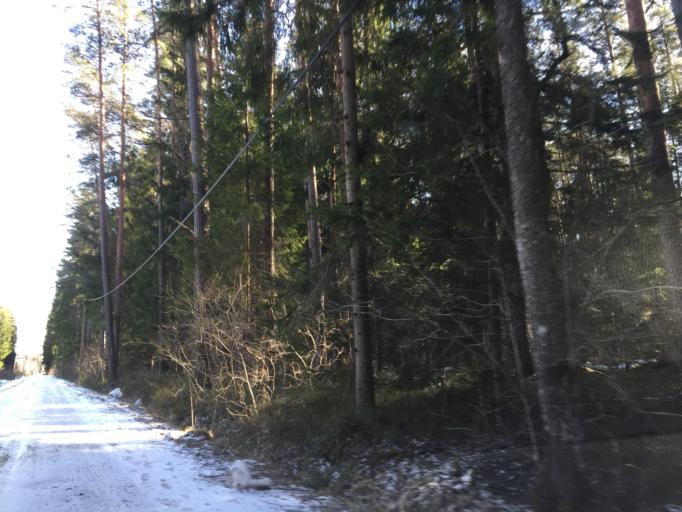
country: LV
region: Garkalne
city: Garkalne
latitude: 56.9521
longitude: 24.4439
